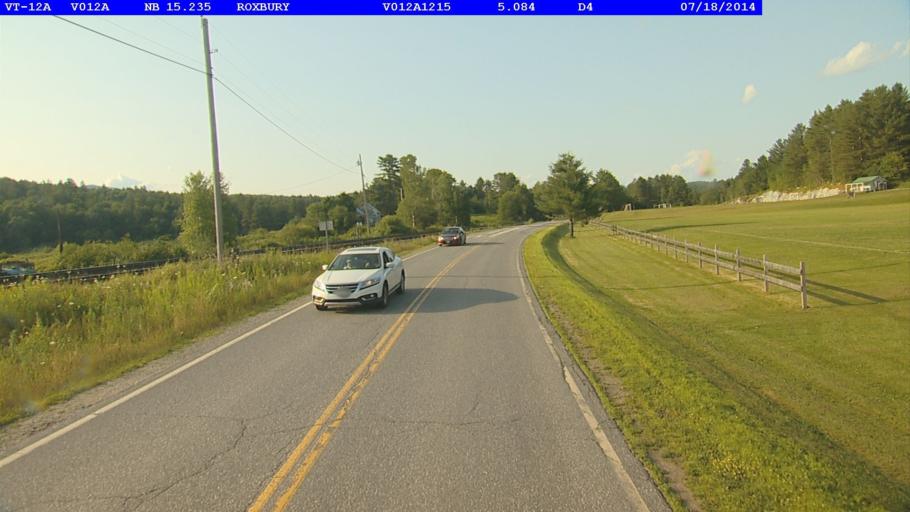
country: US
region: Vermont
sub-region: Washington County
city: Northfield
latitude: 44.0986
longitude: -72.7319
